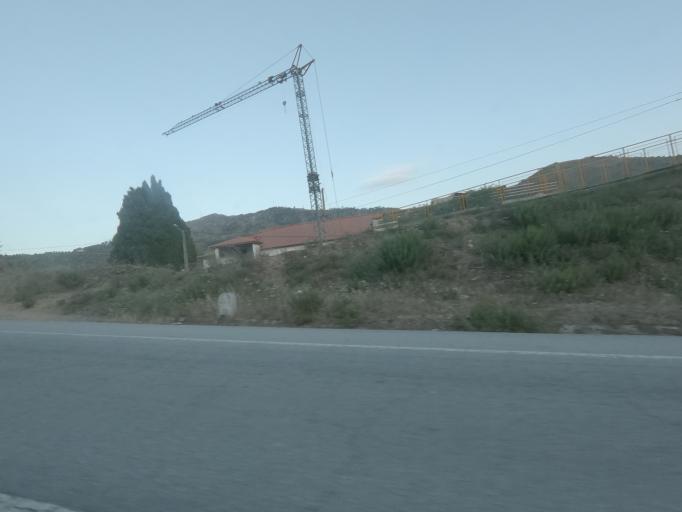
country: PT
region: Vila Real
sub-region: Peso da Regua
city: Peso da Regua
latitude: 41.1319
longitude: -7.7655
